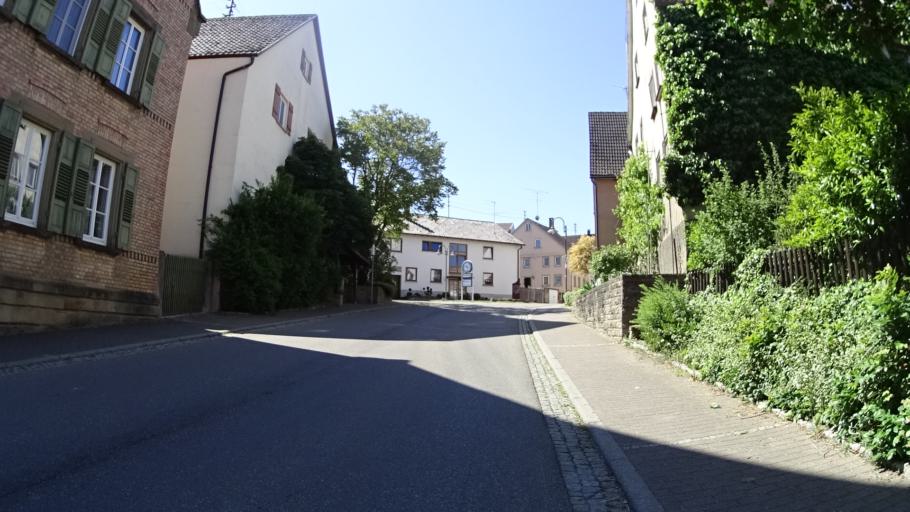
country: DE
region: Baden-Wuerttemberg
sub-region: Regierungsbezirk Stuttgart
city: Weikersheim
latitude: 49.4698
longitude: 9.8725
